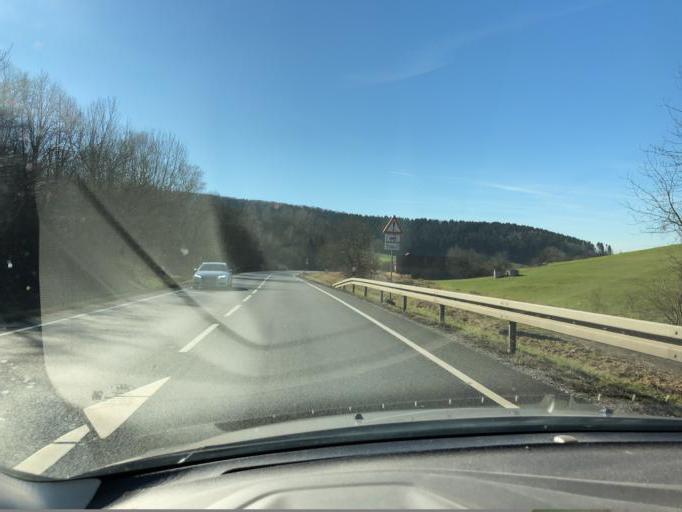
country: DE
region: Lower Saxony
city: Hahausen
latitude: 51.9497
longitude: 10.1841
